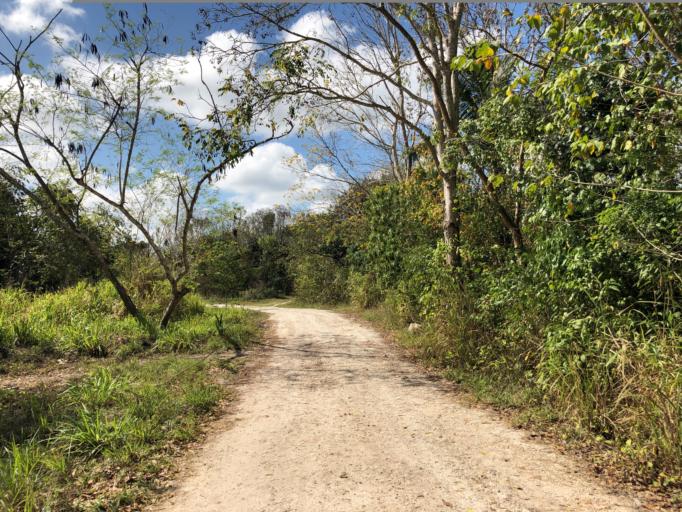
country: MX
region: Quintana Roo
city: Nicolas Bravo
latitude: 18.4453
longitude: -89.3073
